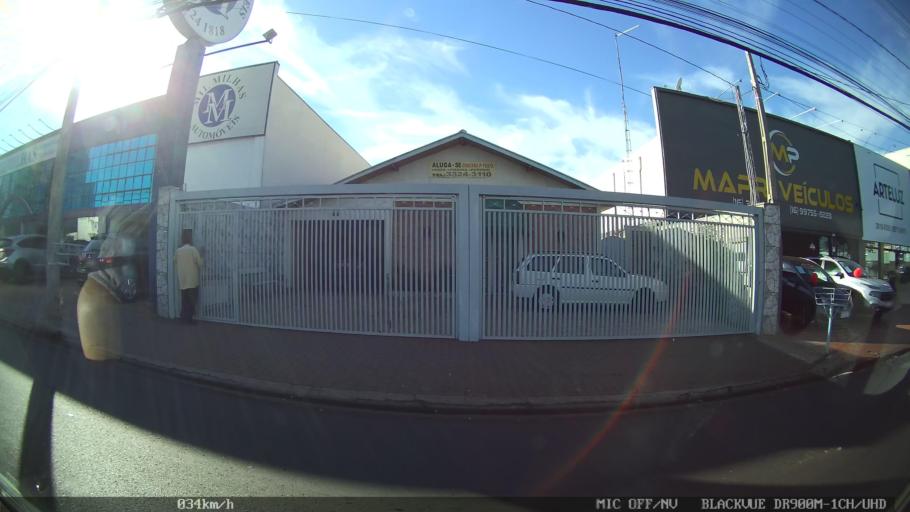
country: BR
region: Sao Paulo
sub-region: Araraquara
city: Araraquara
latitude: -21.7682
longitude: -48.1665
